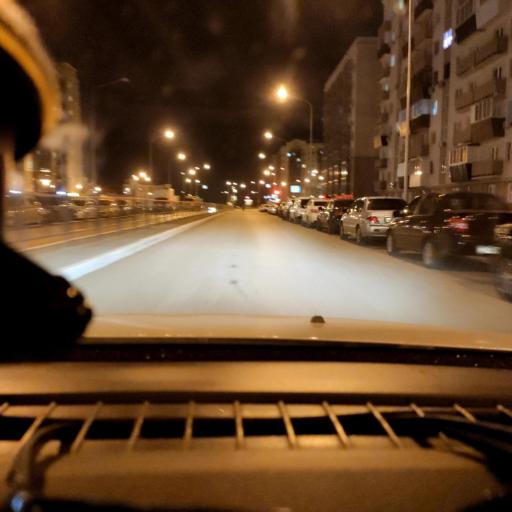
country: RU
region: Samara
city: Samara
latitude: 53.1105
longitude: 50.1446
